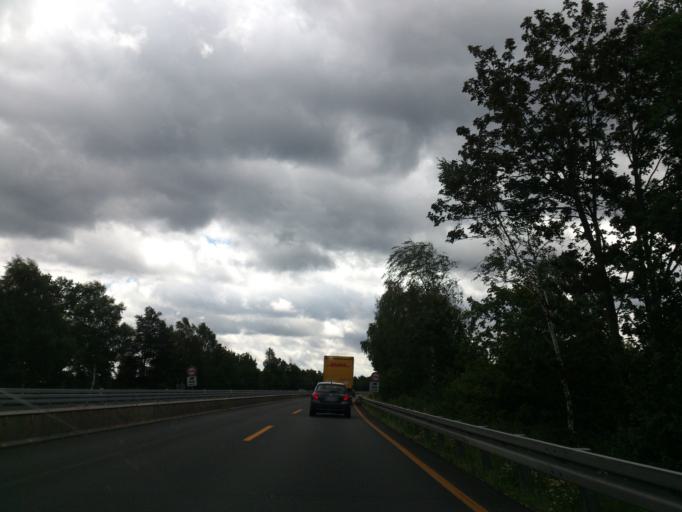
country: DE
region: North Rhine-Westphalia
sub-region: Regierungsbezirk Detmold
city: Hovelhof
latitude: 51.8273
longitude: 8.6983
